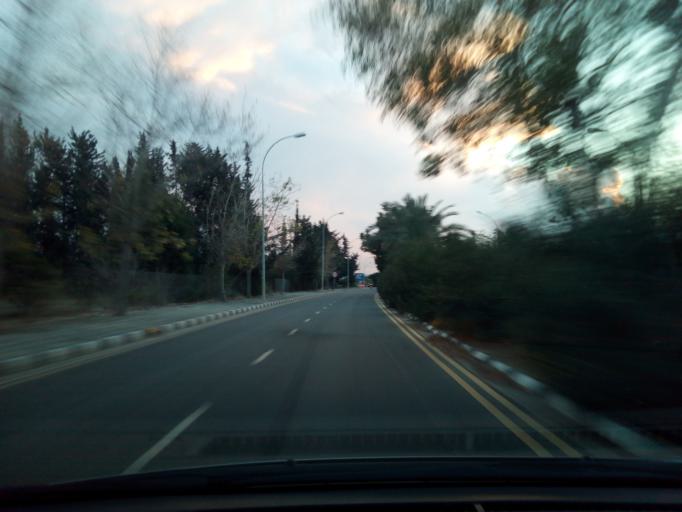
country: CY
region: Pafos
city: Paphos
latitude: 34.7544
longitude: 32.4313
